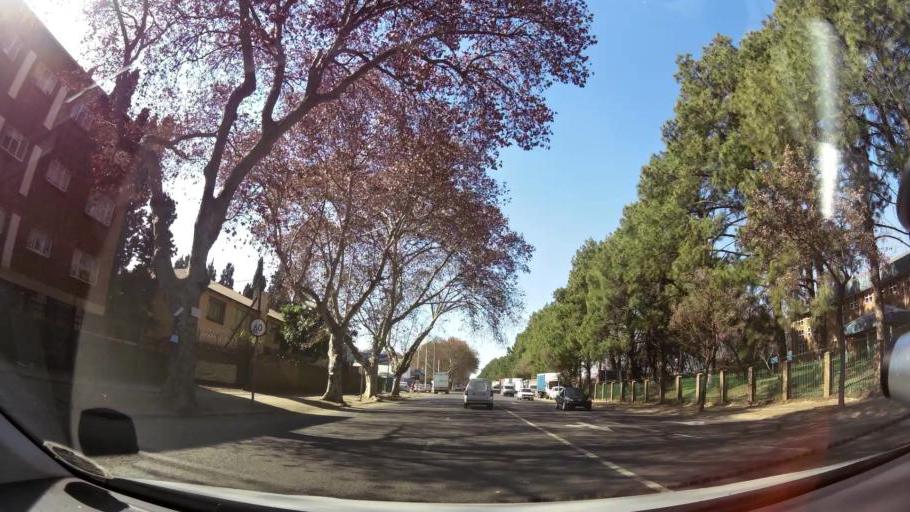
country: ZA
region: Gauteng
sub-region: City of Tshwane Metropolitan Municipality
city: Pretoria
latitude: -25.7482
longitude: 28.1627
